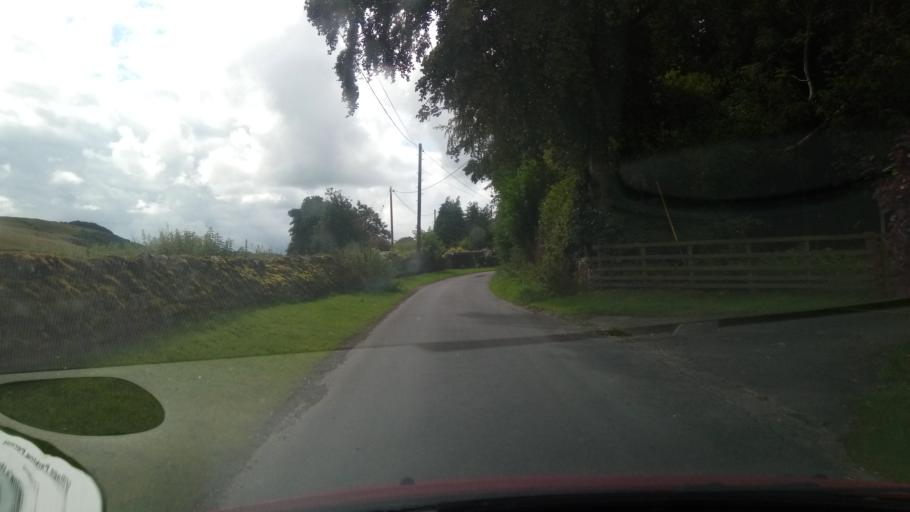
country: GB
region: Scotland
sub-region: The Scottish Borders
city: Hawick
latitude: 55.4198
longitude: -2.7521
